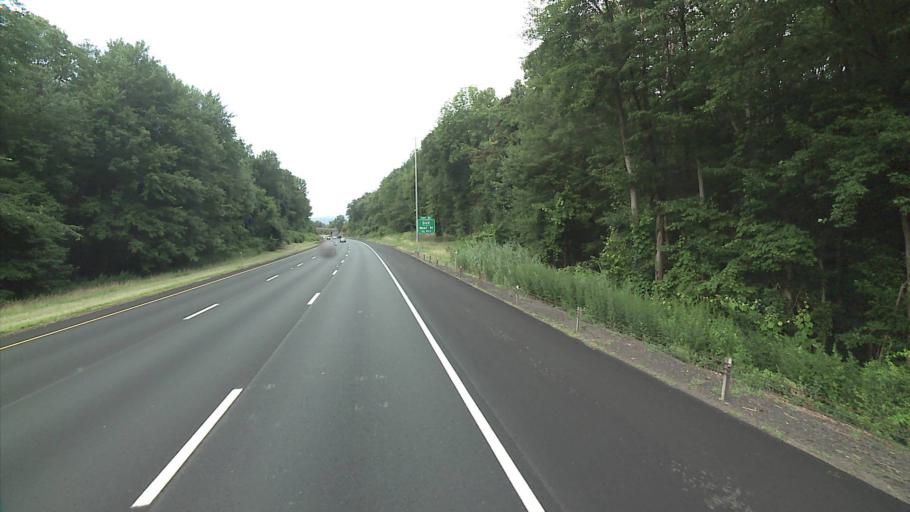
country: US
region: Connecticut
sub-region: Hartford County
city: Plainville
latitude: 41.6217
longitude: -72.8904
